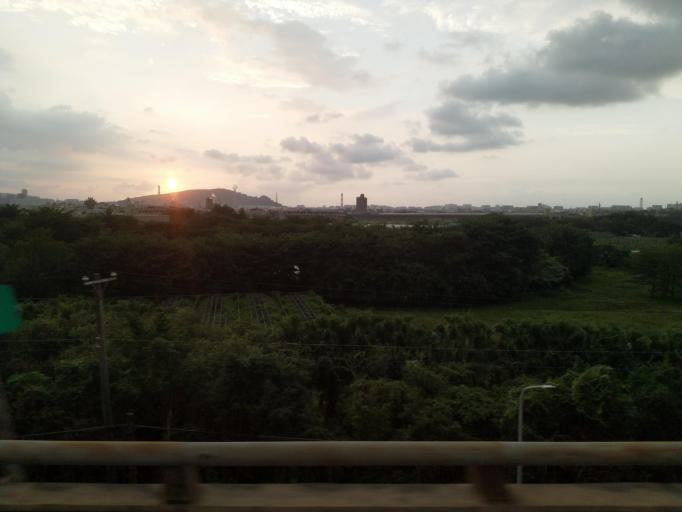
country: TW
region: Taiwan
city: Fengshan
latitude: 22.7055
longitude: 120.3602
